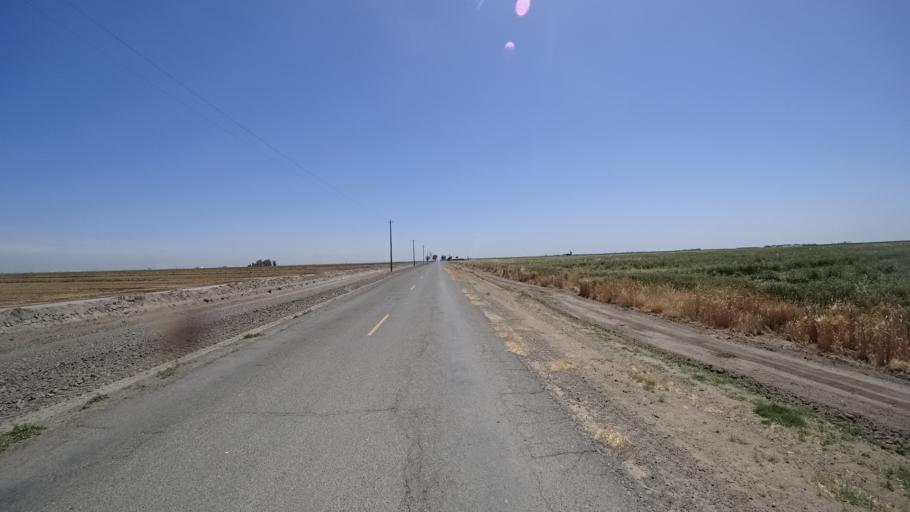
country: US
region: California
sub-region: Kings County
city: Corcoran
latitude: 36.1379
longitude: -119.6609
